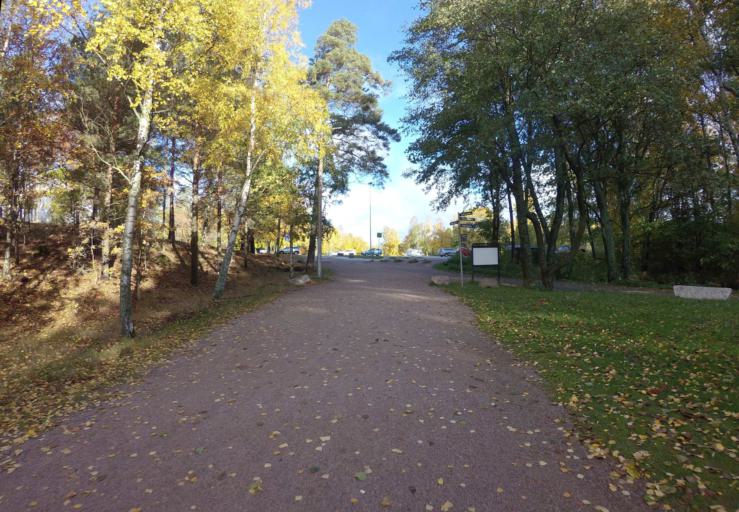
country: FI
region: Varsinais-Suomi
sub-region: Turku
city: Naantali
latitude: 60.4221
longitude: 22.0952
